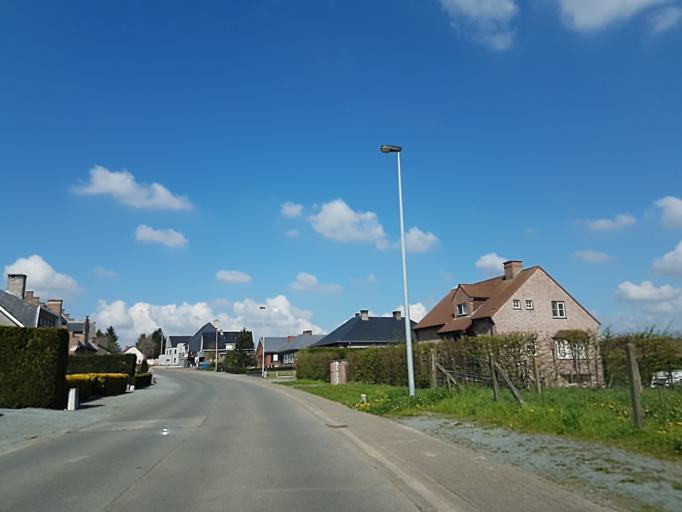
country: BE
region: Flanders
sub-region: Provincie Oost-Vlaanderen
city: Sint-Maria-Lierde
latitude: 50.8132
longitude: 3.8237
